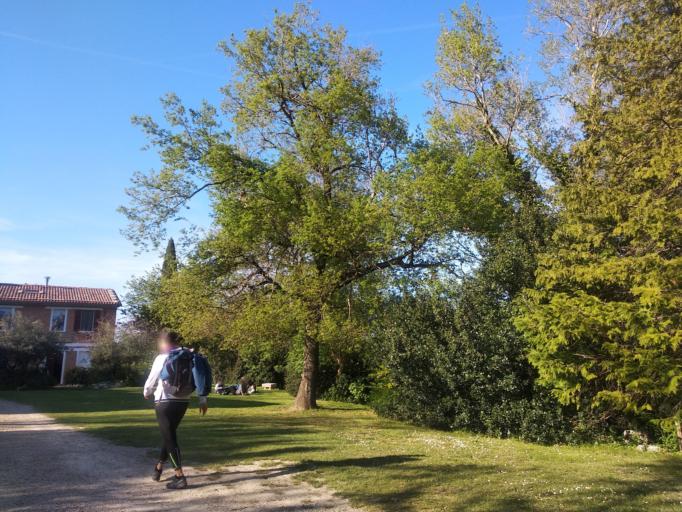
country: IT
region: Emilia-Romagna
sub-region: Provincia di Ravenna
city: Fognano
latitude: 44.2266
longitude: 11.7378
